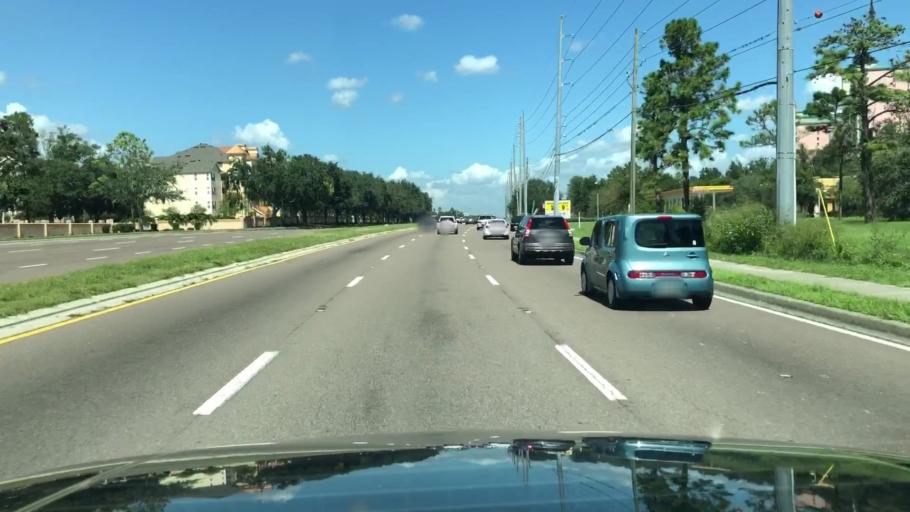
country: US
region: Florida
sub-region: Osceola County
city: Celebration
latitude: 28.3644
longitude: -81.5019
